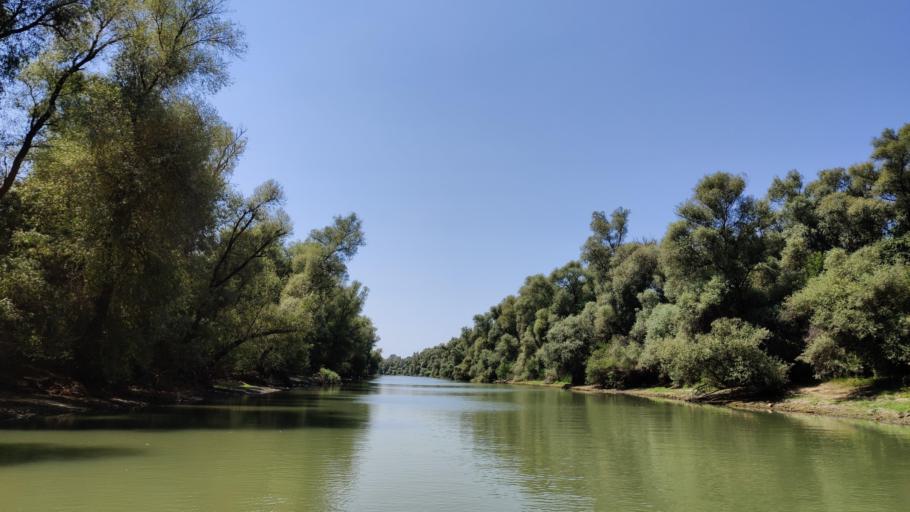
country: RO
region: Tulcea
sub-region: Comuna Nufaru
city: Nufaru
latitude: 45.2300
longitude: 28.8980
